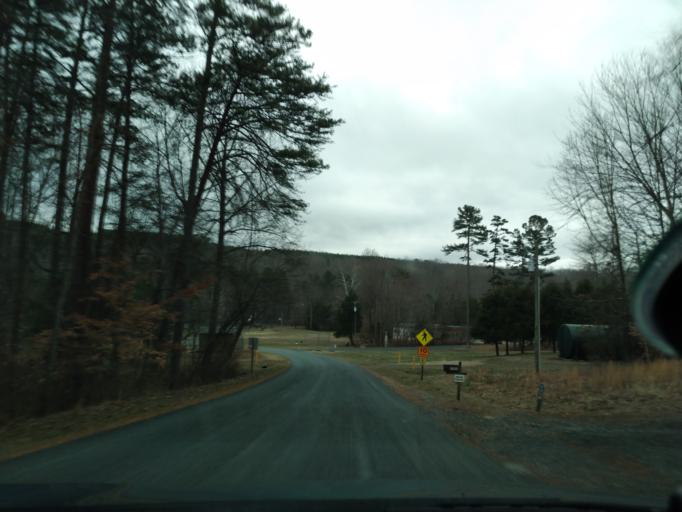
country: US
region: Virginia
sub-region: Buckingham County
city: Buckingham
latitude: 37.3909
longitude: -78.6428
